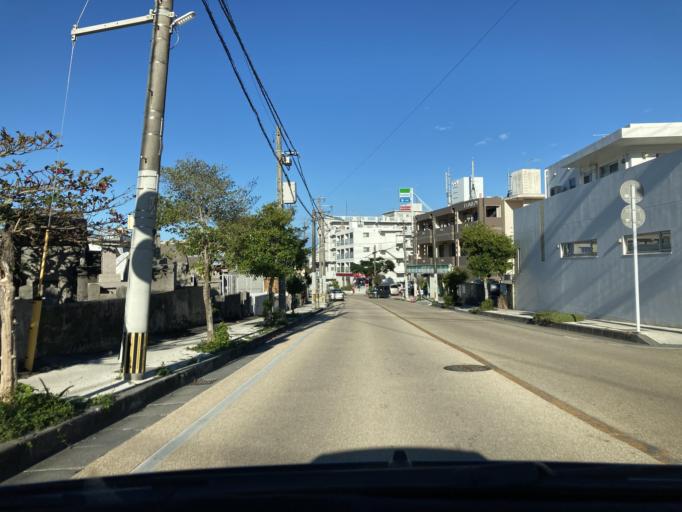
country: JP
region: Okinawa
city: Naha-shi
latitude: 26.2090
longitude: 127.7151
